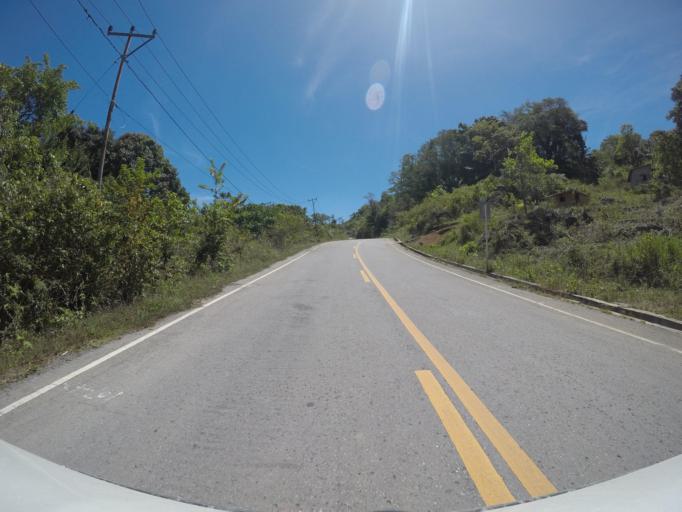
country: TL
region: Manatuto
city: Manatuto
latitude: -8.8030
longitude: 125.9687
